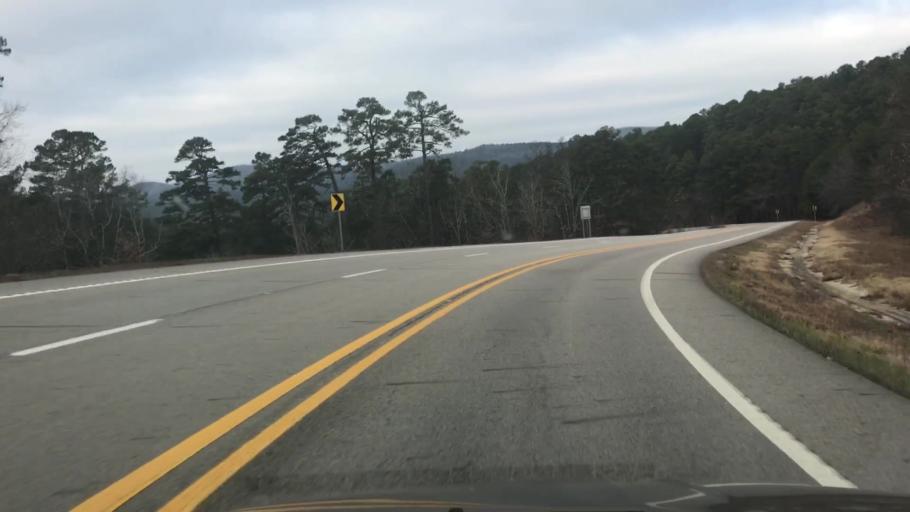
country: US
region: Arkansas
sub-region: Montgomery County
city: Mount Ida
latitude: 34.6819
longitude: -93.7970
